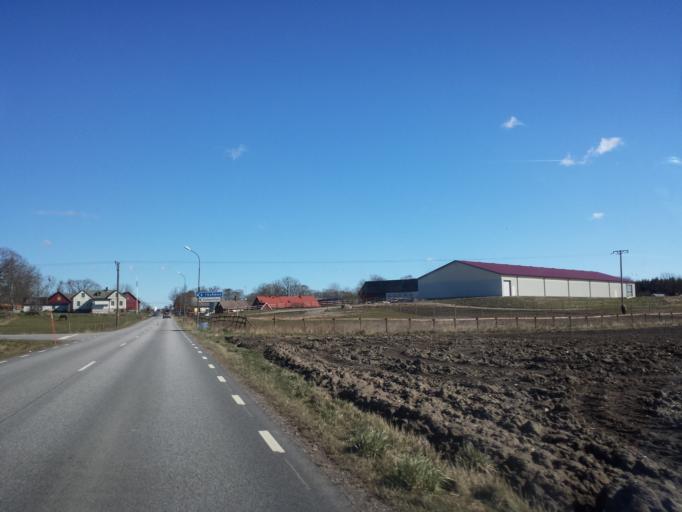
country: SE
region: Skane
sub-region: Tomelilla Kommun
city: Tomelilla
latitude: 55.6439
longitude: 13.8873
